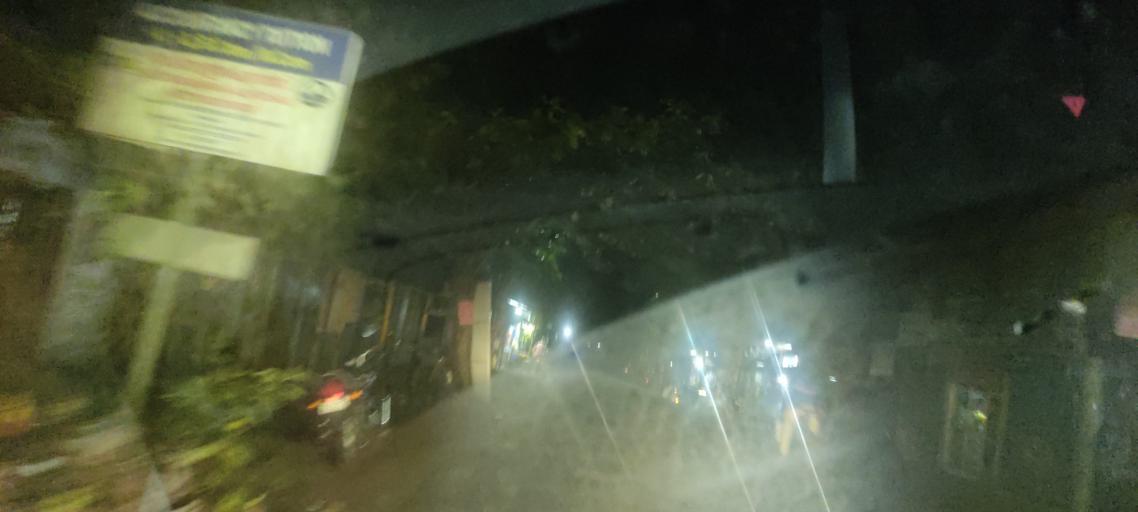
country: IN
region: Kerala
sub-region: Alappuzha
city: Vayalar
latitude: 9.7214
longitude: 76.3375
